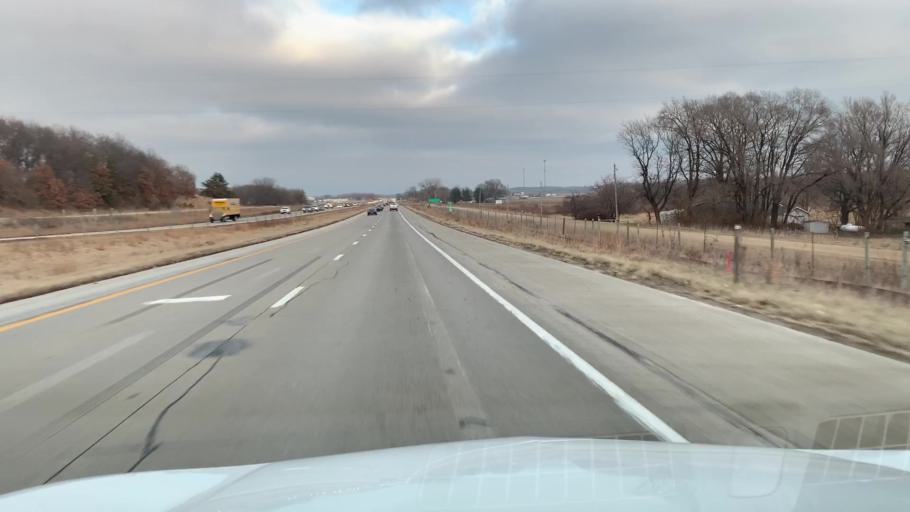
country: US
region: Iowa
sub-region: Jasper County
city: Colfax
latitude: 41.6870
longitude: -93.2706
